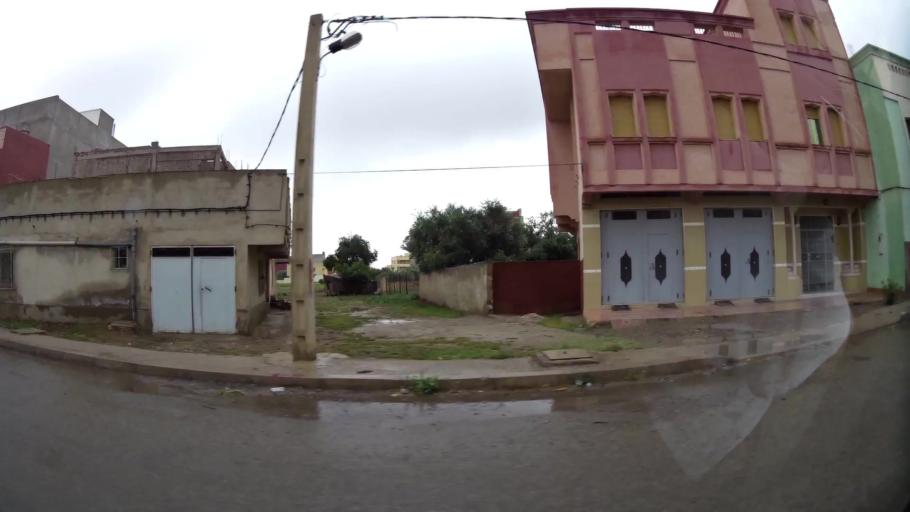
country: MA
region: Oriental
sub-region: Nador
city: Nador
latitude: 35.1573
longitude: -2.9728
